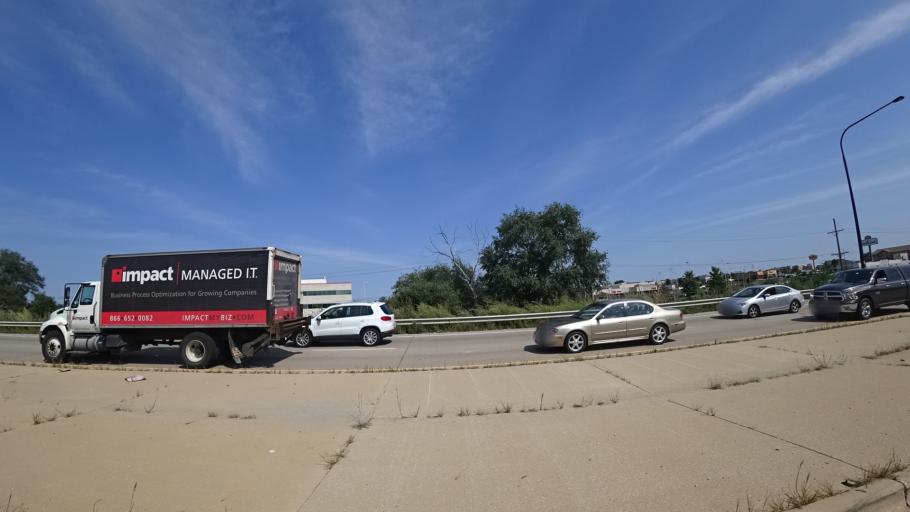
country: US
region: Illinois
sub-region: Cook County
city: Orland Hills
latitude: 41.5448
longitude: -87.8510
